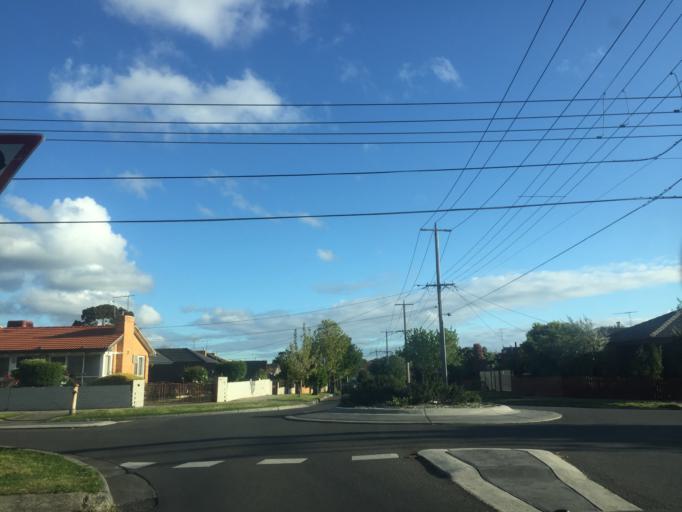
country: AU
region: Victoria
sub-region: Darebin
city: Kingsbury
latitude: -37.7315
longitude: 145.0339
